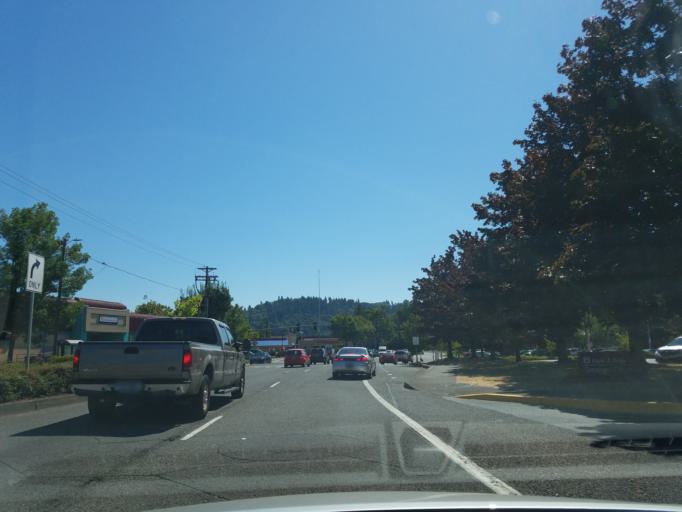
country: US
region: Oregon
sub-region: Multnomah County
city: Gresham
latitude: 45.5055
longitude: -122.4354
